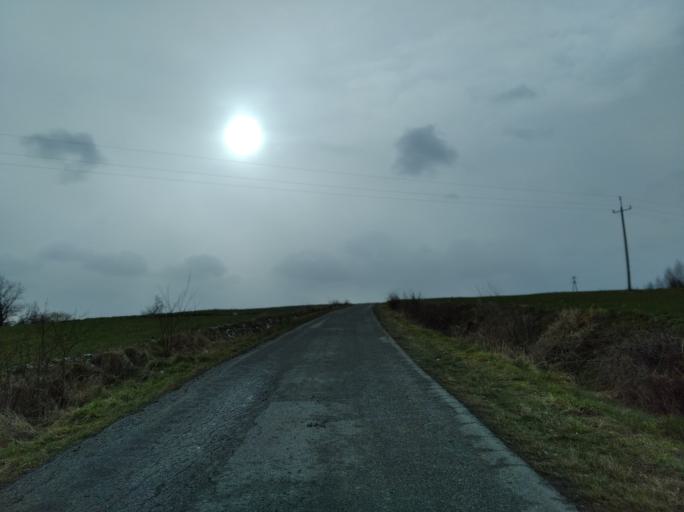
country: PL
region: Subcarpathian Voivodeship
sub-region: Powiat strzyzowski
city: Strzyzow
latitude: 49.8968
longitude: 21.7370
